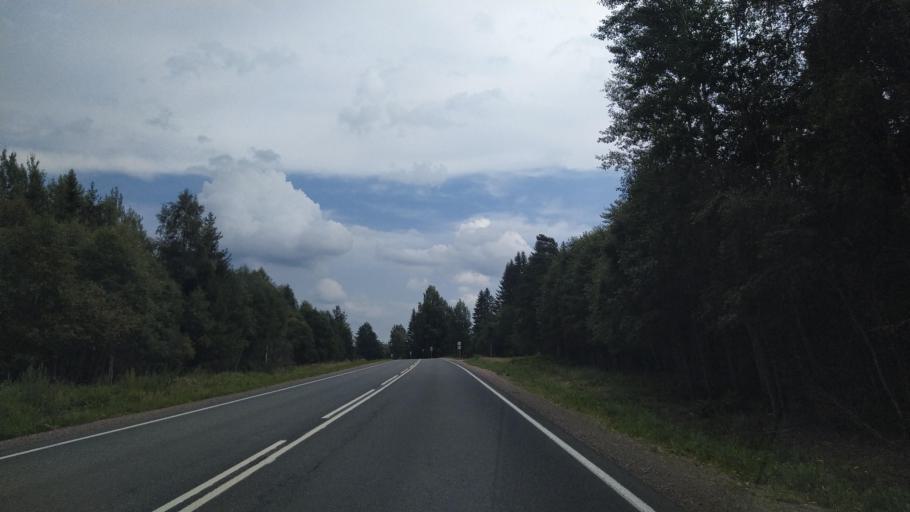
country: RU
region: Pskov
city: Pskov
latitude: 57.8131
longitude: 28.6829
